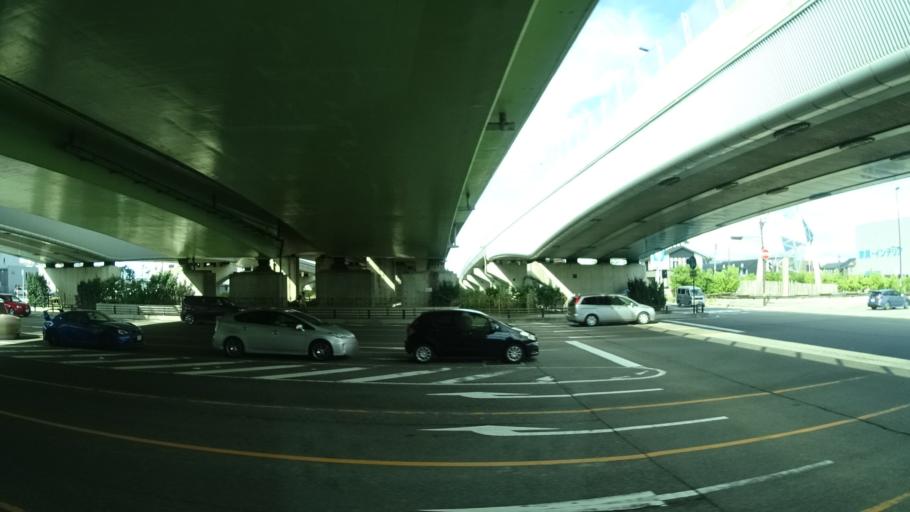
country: JP
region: Ishikawa
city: Kanazawa-shi
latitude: 36.5913
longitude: 136.6310
